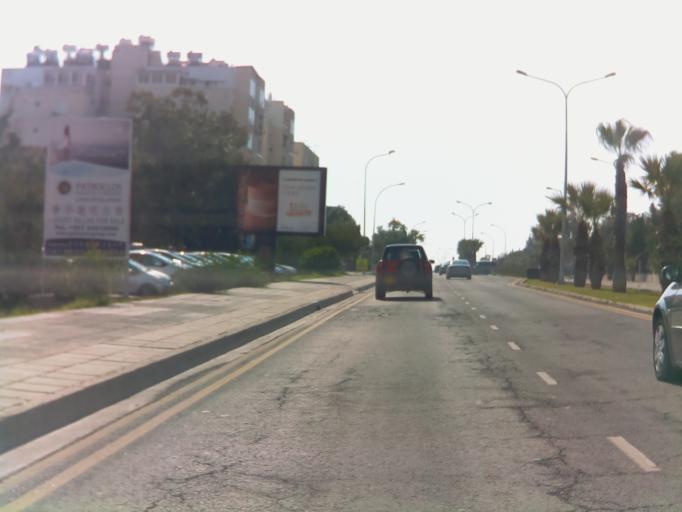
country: CY
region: Larnaka
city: Larnaca
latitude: 34.9032
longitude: 33.6304
